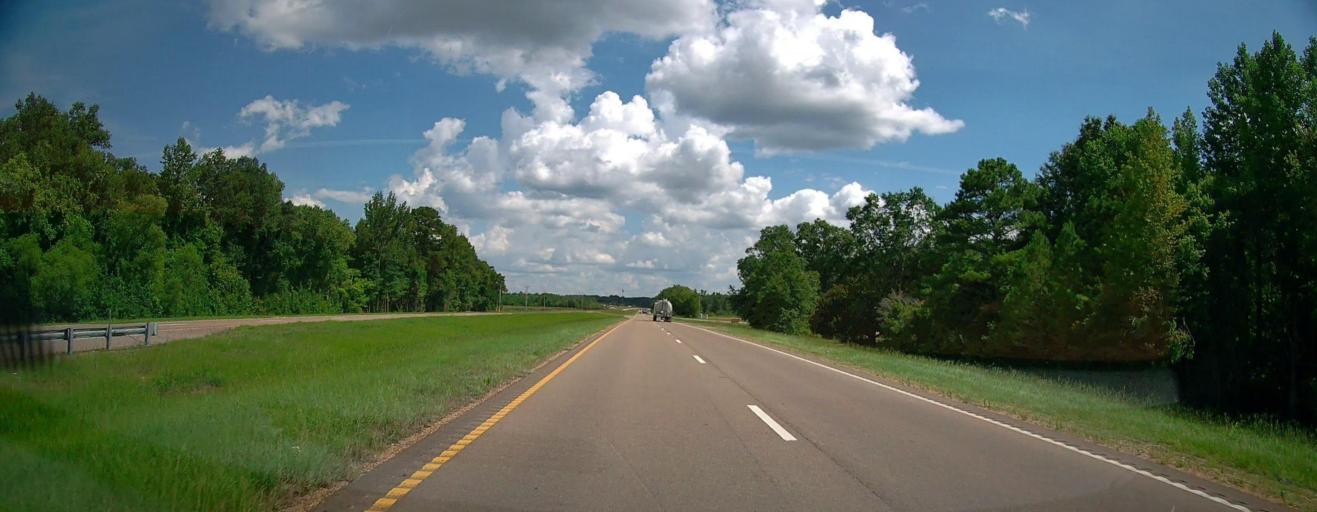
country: US
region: Mississippi
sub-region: Lowndes County
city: Columbus Air Force Base
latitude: 33.6679
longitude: -88.4260
